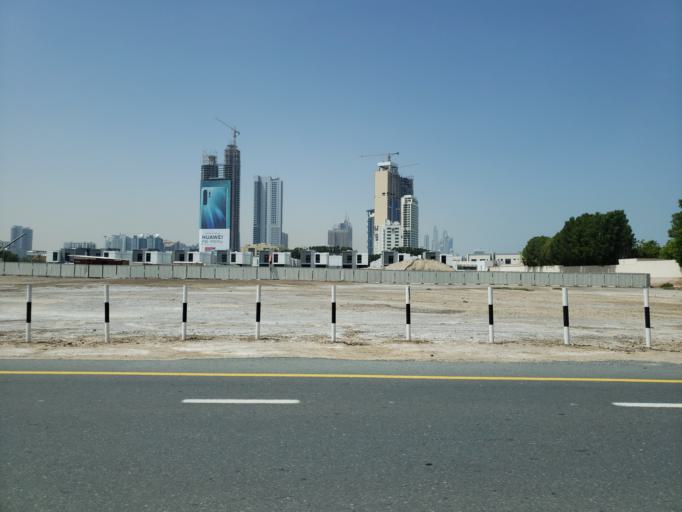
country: AE
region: Dubai
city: Dubai
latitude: 25.1161
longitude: 55.1841
